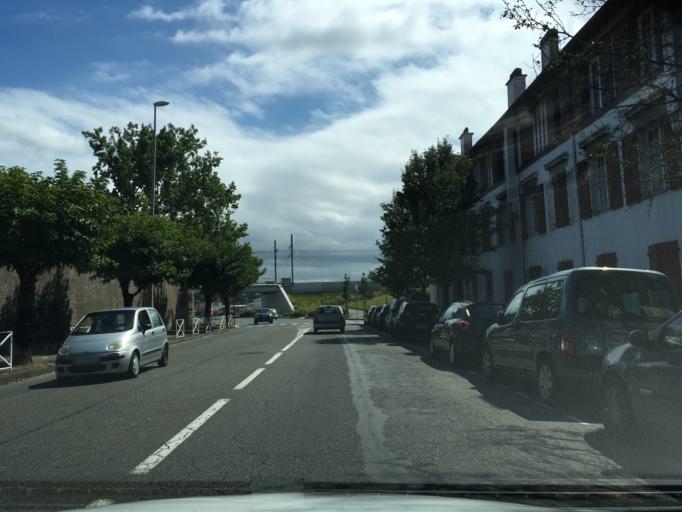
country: FR
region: Aquitaine
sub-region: Departement des Pyrenees-Atlantiques
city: Bayonne
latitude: 43.4912
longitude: -1.4634
